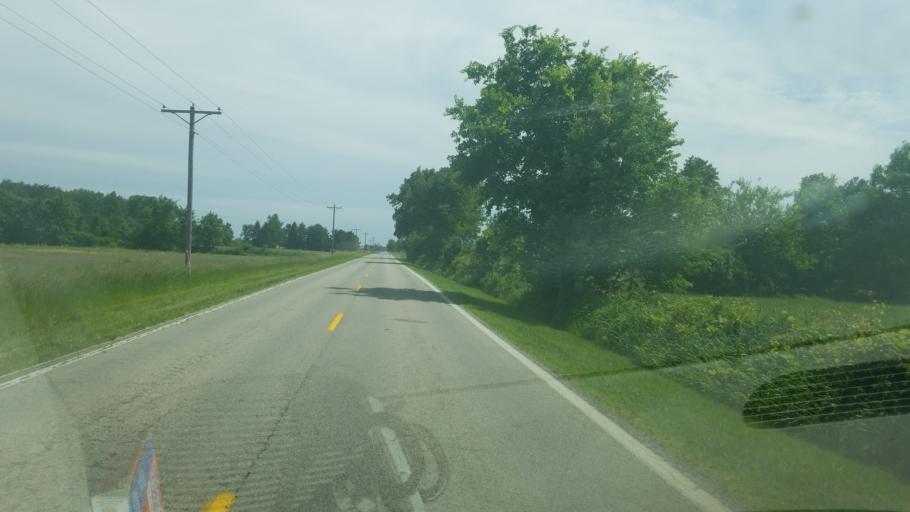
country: US
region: Ohio
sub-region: Morrow County
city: Cardington
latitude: 40.5082
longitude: -82.9629
